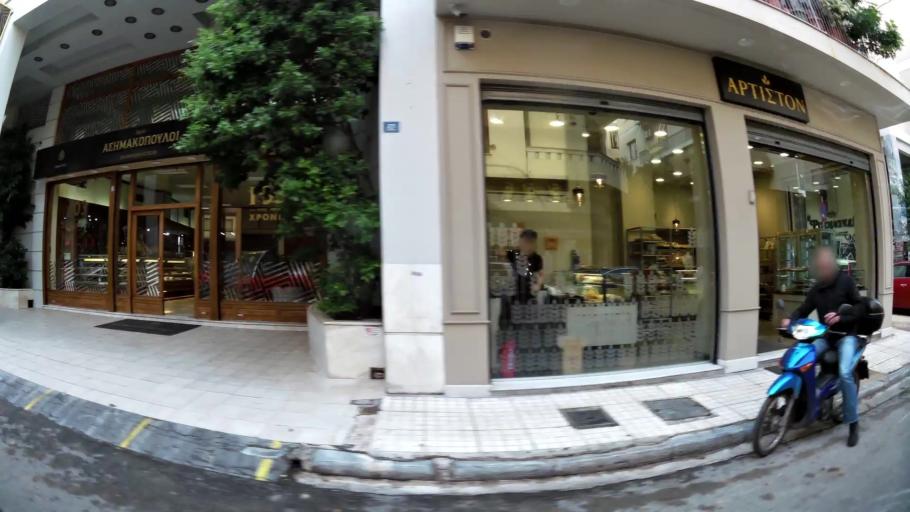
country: GR
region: Attica
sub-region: Nomarchia Athinas
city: Kipseli
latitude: 37.9854
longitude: 23.7382
